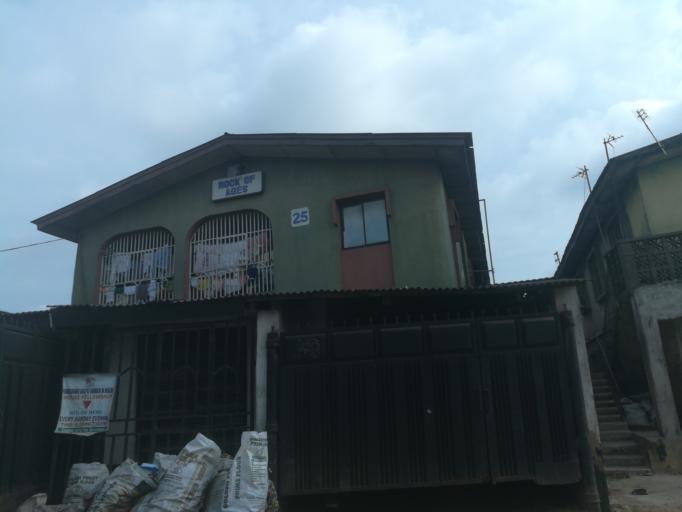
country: NG
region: Lagos
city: Agege
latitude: 6.6138
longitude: 3.3230
